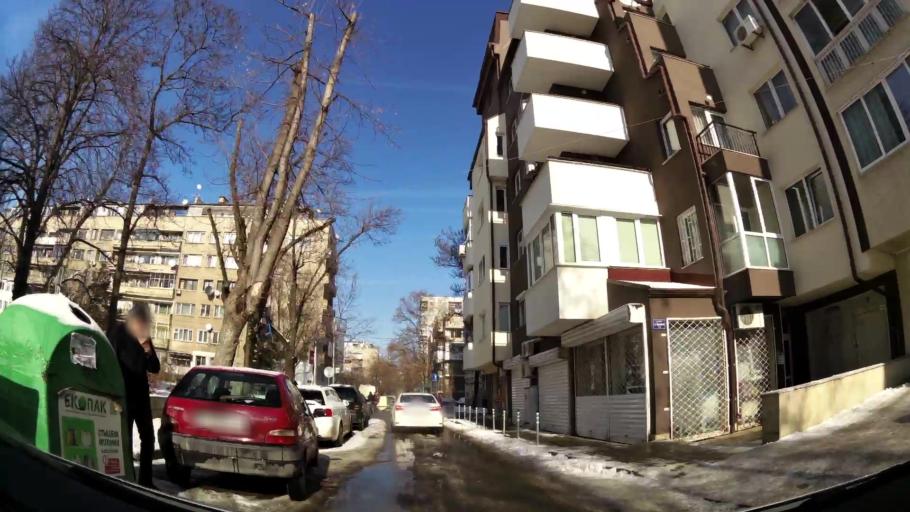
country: BG
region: Sofia-Capital
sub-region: Stolichna Obshtina
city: Sofia
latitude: 42.6760
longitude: 23.3083
